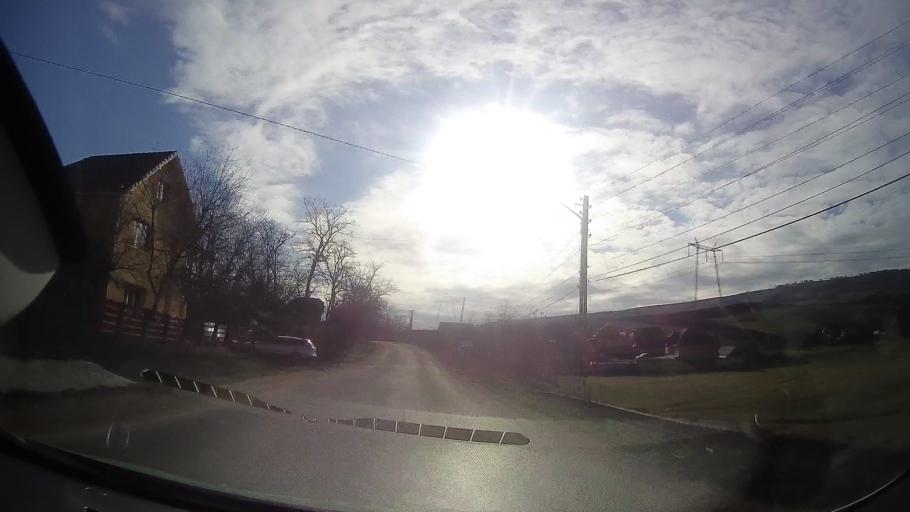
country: RO
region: Mures
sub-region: Comuna Valea Larga
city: Valea Larga
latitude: 46.6121
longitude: 24.0896
